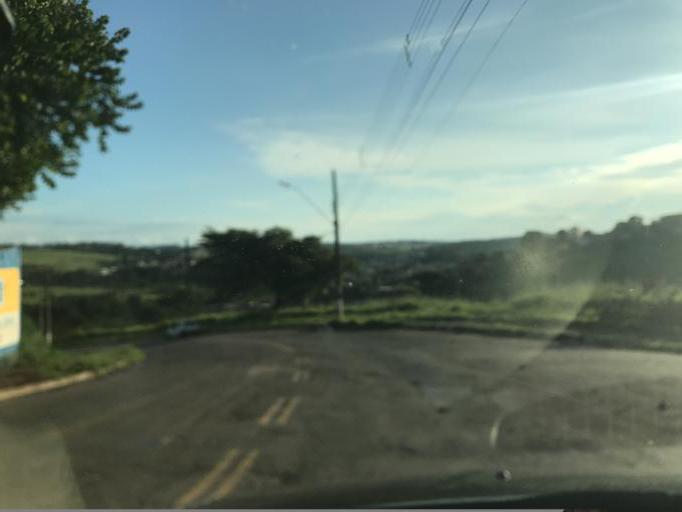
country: BR
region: Minas Gerais
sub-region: Tres Coracoes
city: Tres Coracoes
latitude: -21.6954
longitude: -45.2452
